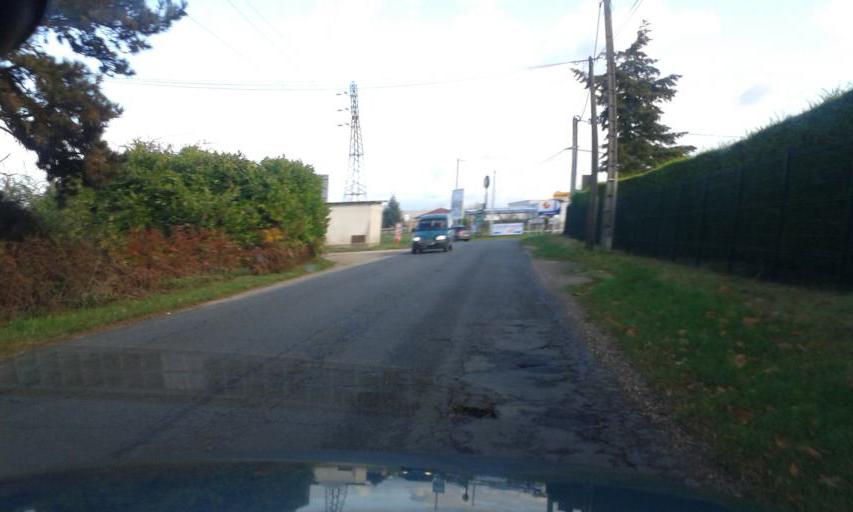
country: FR
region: Centre
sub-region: Departement du Loiret
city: Olivet
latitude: 47.8393
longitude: 1.9126
